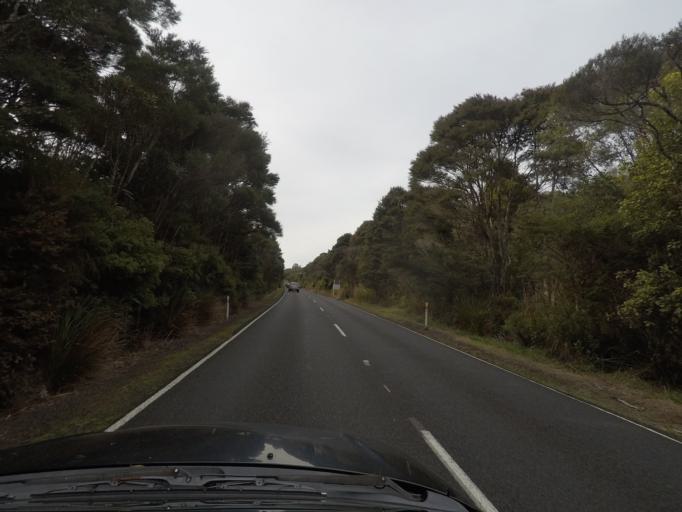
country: NZ
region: Auckland
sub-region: Auckland
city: Titirangi
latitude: -36.9359
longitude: 174.5602
